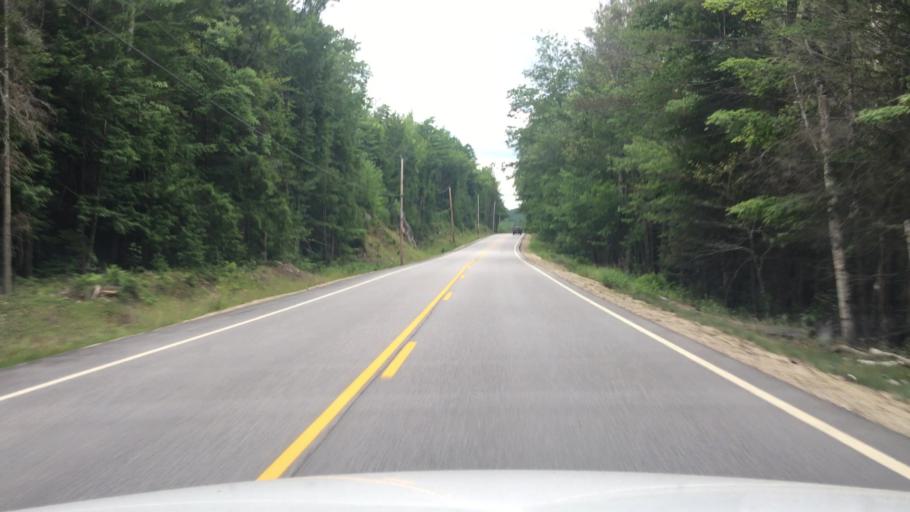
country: US
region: Maine
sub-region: Oxford County
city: Hartford
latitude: 44.3608
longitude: -70.3603
